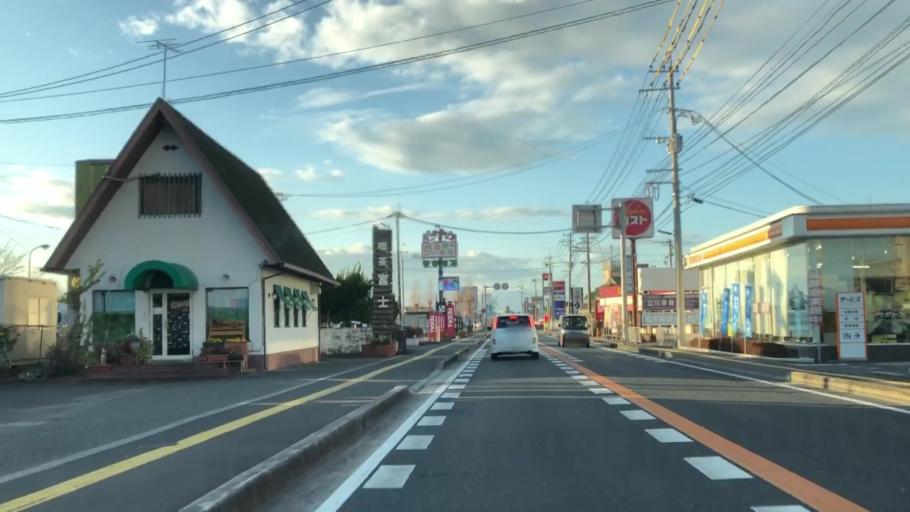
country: JP
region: Oita
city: Bungo-Takada-shi
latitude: 33.5273
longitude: 131.3408
